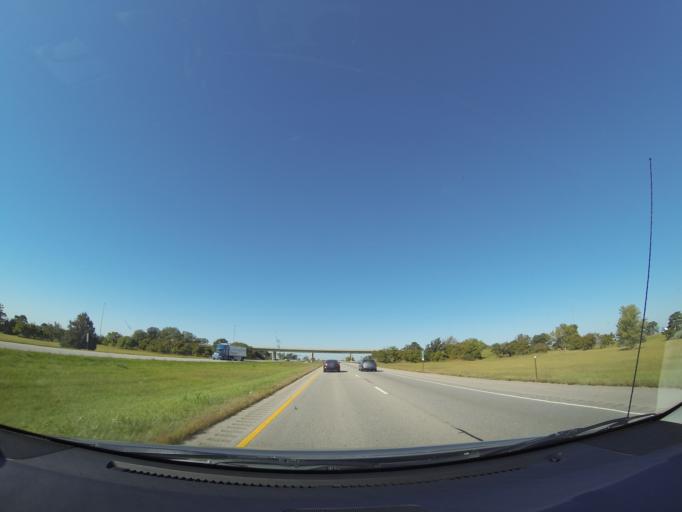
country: US
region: Nebraska
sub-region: Seward County
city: Milford
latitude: 40.8223
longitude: -97.0998
